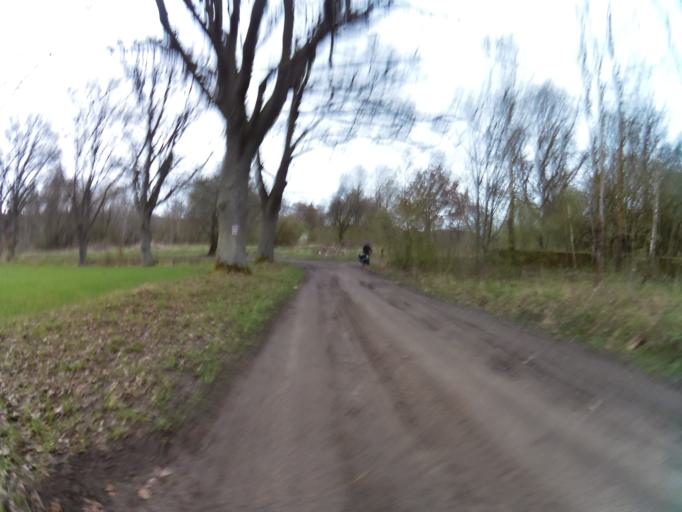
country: PL
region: West Pomeranian Voivodeship
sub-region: Powiat szczecinecki
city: Borne Sulinowo
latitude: 53.6600
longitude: 16.5400
